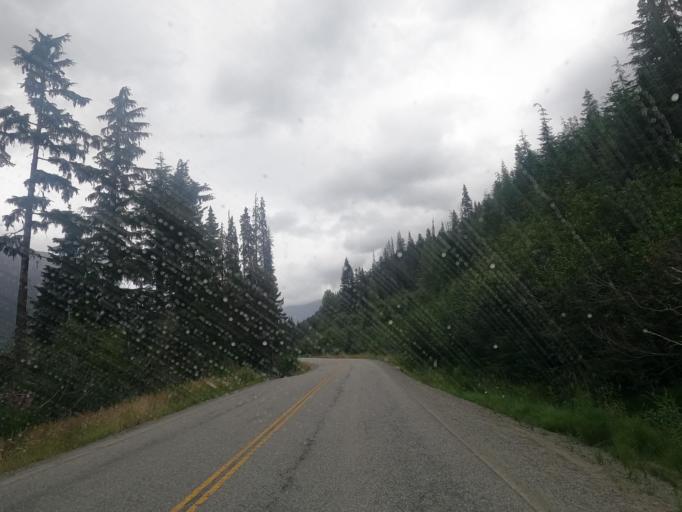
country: CA
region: British Columbia
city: Lillooet
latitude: 50.3990
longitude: -122.3151
